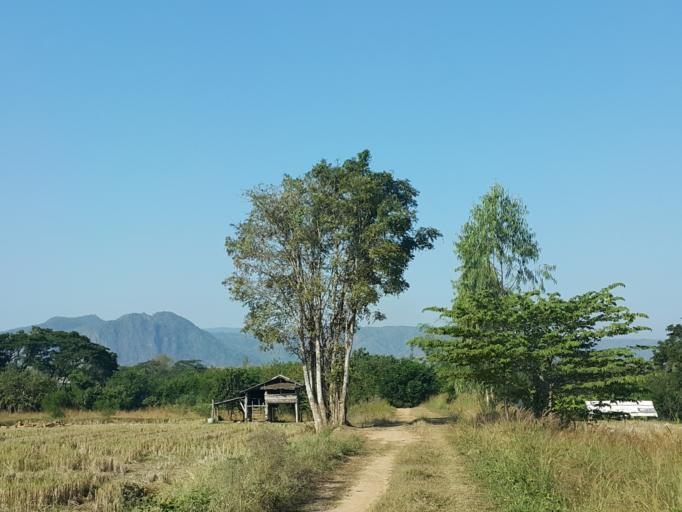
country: TH
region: Sukhothai
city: Thung Saliam
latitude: 17.3190
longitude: 99.4314
